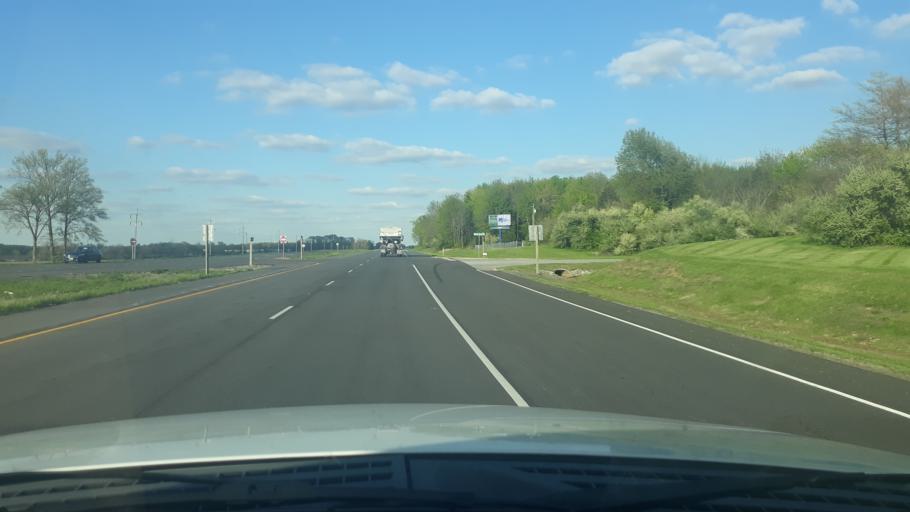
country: US
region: Illinois
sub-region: Saline County
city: Eldorado
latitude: 37.7908
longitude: -88.4787
